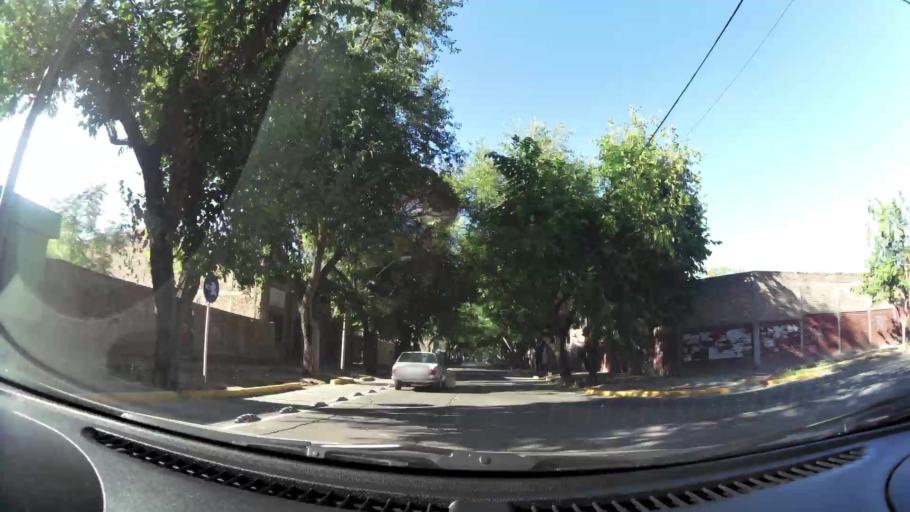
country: AR
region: Mendoza
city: Las Heras
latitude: -32.8689
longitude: -68.8257
